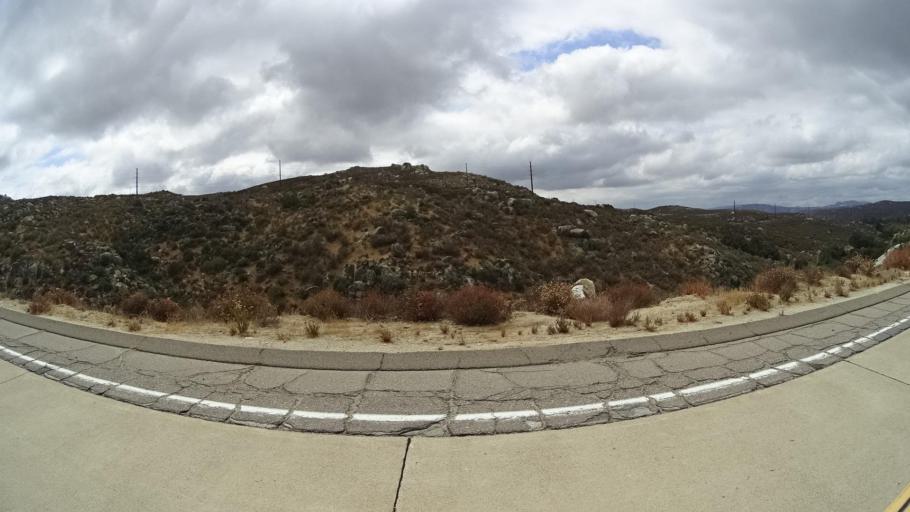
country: US
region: California
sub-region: San Diego County
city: Campo
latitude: 32.7051
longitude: -116.3733
